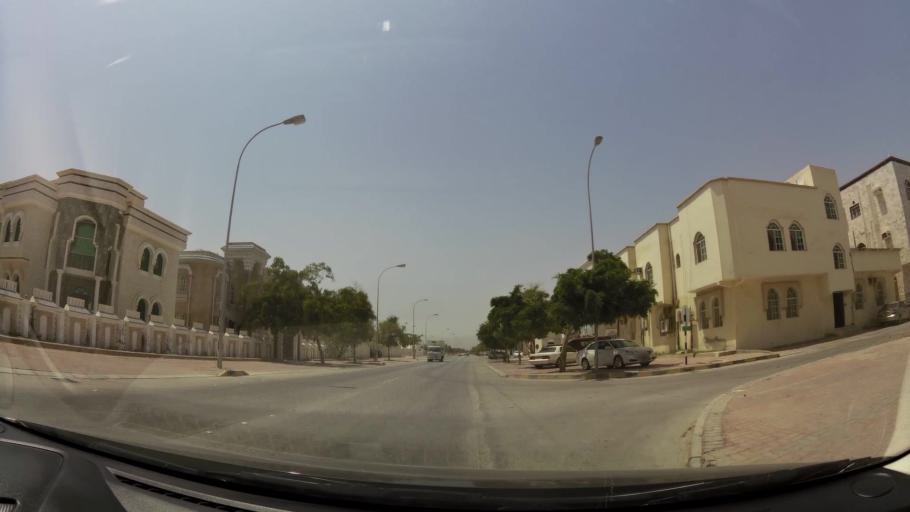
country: OM
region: Zufar
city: Salalah
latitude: 17.0153
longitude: 54.0757
